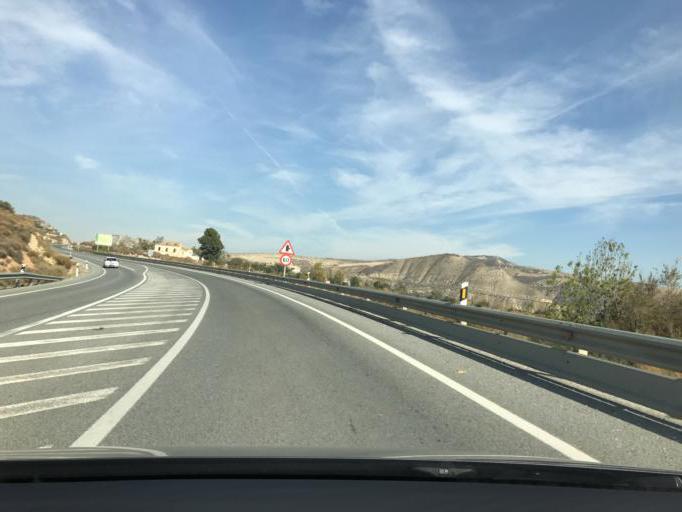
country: ES
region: Andalusia
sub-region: Provincia de Granada
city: Las Gabias
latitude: 37.1011
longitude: -3.7295
